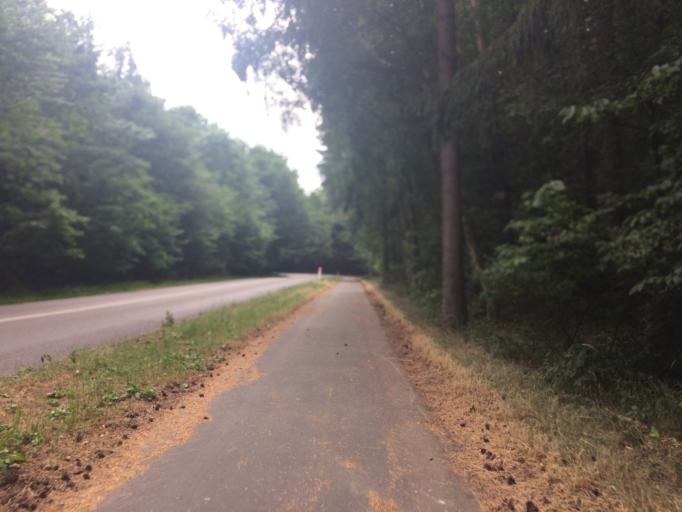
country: DK
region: Capital Region
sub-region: Bornholm Kommune
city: Ronne
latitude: 55.1586
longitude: 14.7151
